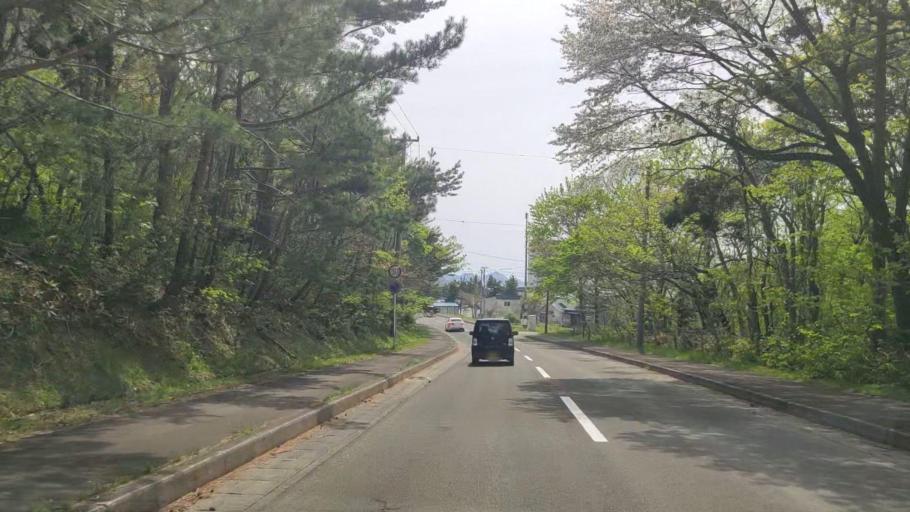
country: JP
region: Aomori
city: Aomori Shi
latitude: 40.9000
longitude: 140.8633
